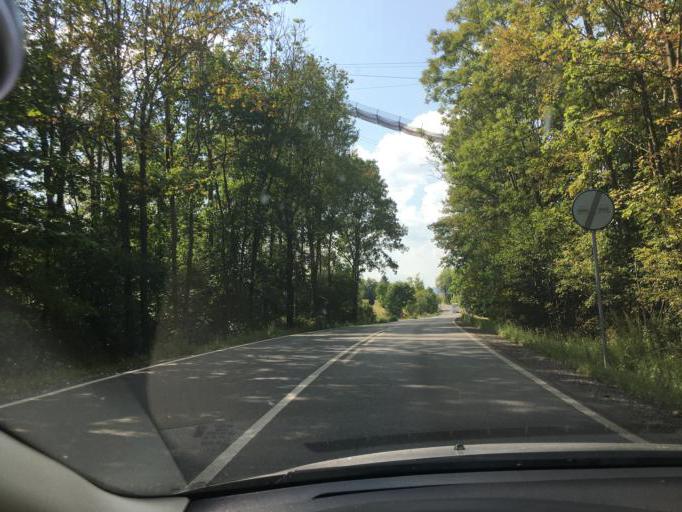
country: CZ
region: Kralovehradecky
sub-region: Okres Trutnov
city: Rudnik
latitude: 50.6126
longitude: 15.6893
